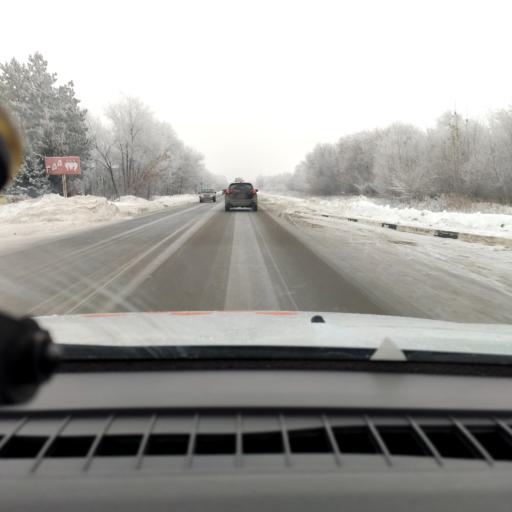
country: RU
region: Samara
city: Samara
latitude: 53.0850
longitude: 50.1588
